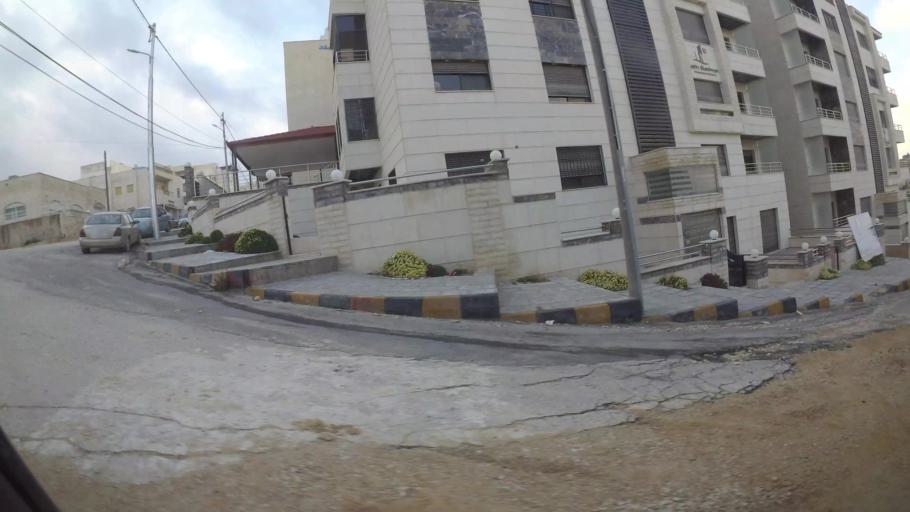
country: JO
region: Amman
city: Al Jubayhah
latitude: 32.0494
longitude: 35.8952
